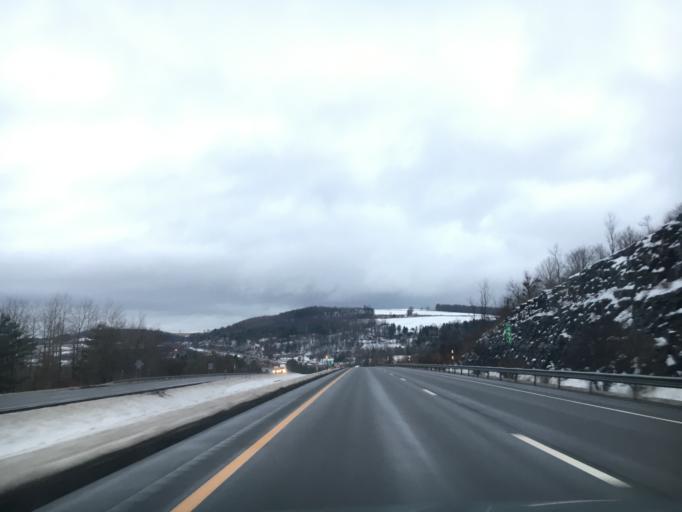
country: US
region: New York
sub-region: Cortland County
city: McGraw
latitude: 42.5826
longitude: -76.1248
